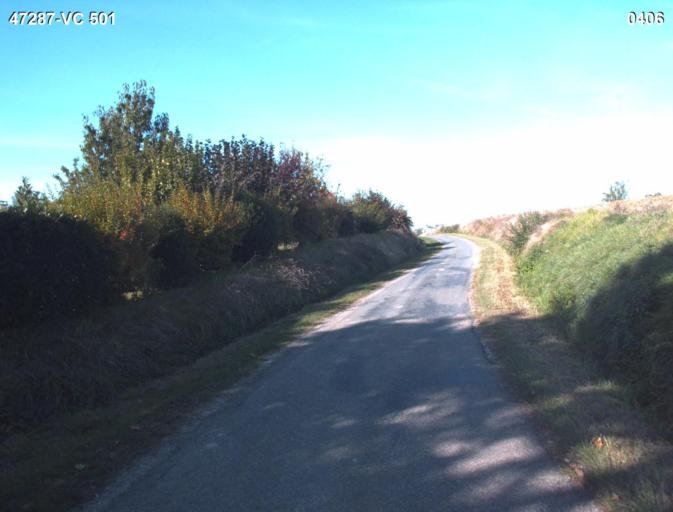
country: FR
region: Aquitaine
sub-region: Departement du Lot-et-Garonne
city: Laplume
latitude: 44.1164
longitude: 0.4584
